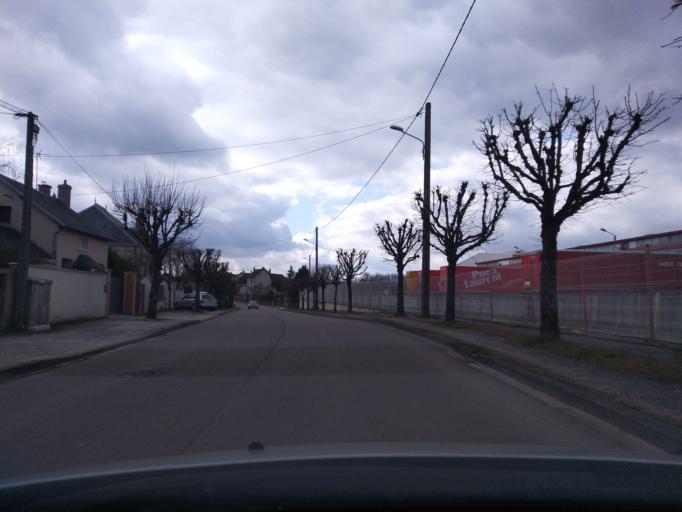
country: FR
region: Bourgogne
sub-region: Departement de l'Yonne
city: Avallon
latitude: 47.4939
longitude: 3.9215
